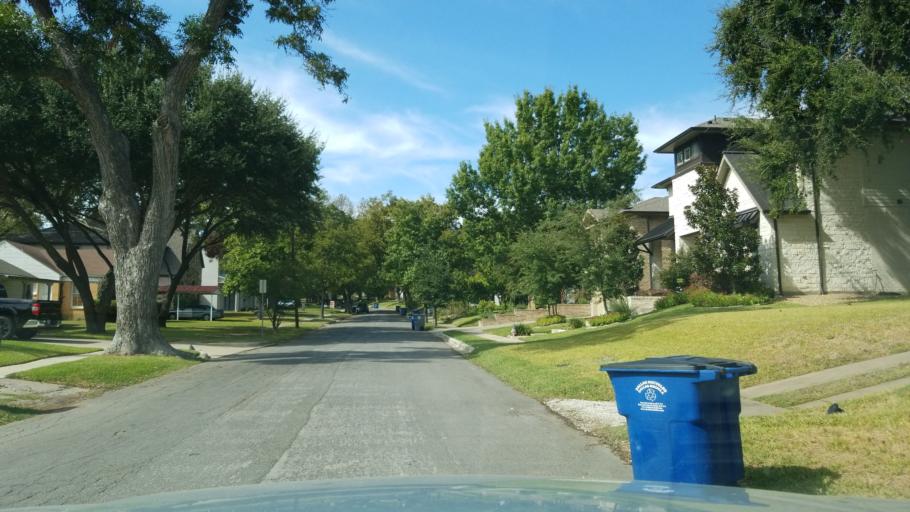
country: US
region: Texas
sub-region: Dallas County
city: Highland Park
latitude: 32.8109
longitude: -96.7329
